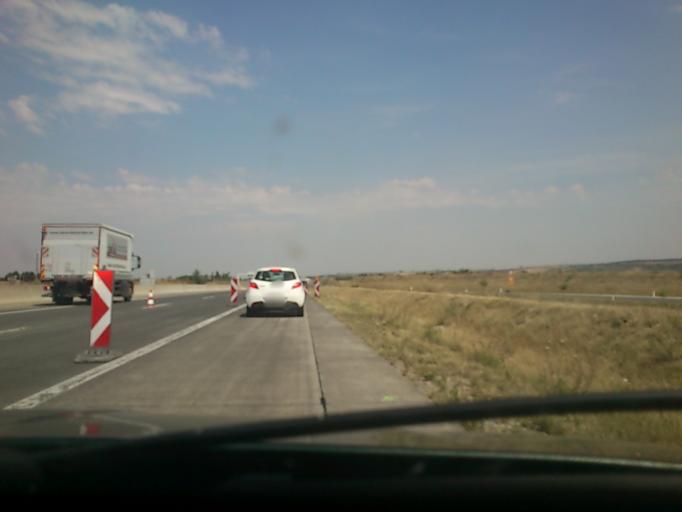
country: AT
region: Lower Austria
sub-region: Politischer Bezirk Mistelbach
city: Grossebersdorf
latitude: 48.3730
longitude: 16.4886
